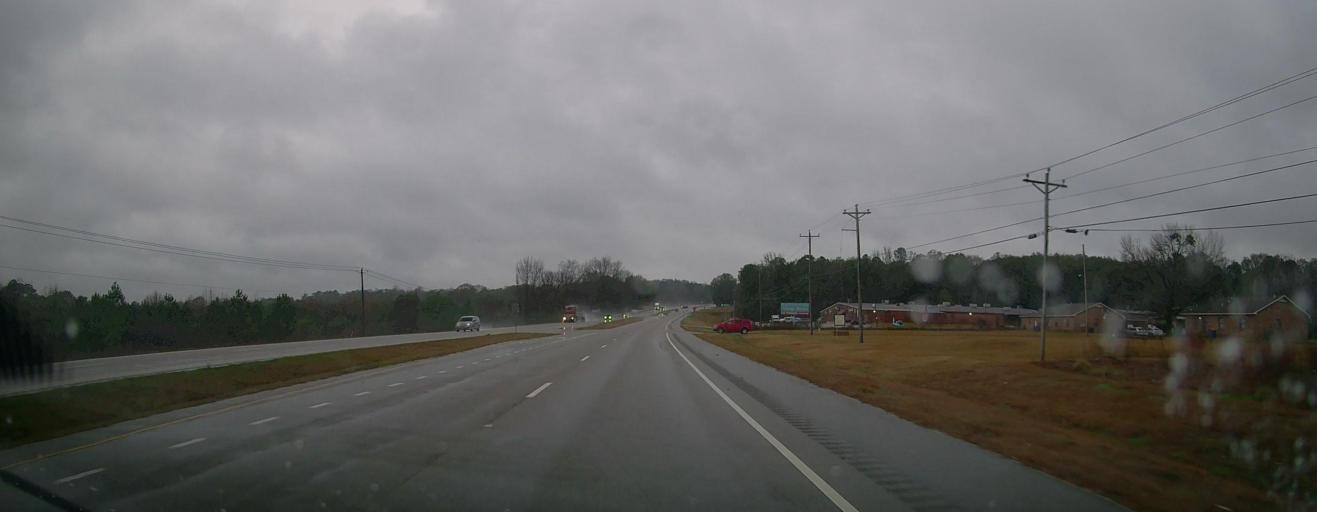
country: US
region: Alabama
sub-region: Autauga County
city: Prattville
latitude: 32.4458
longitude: -86.4851
